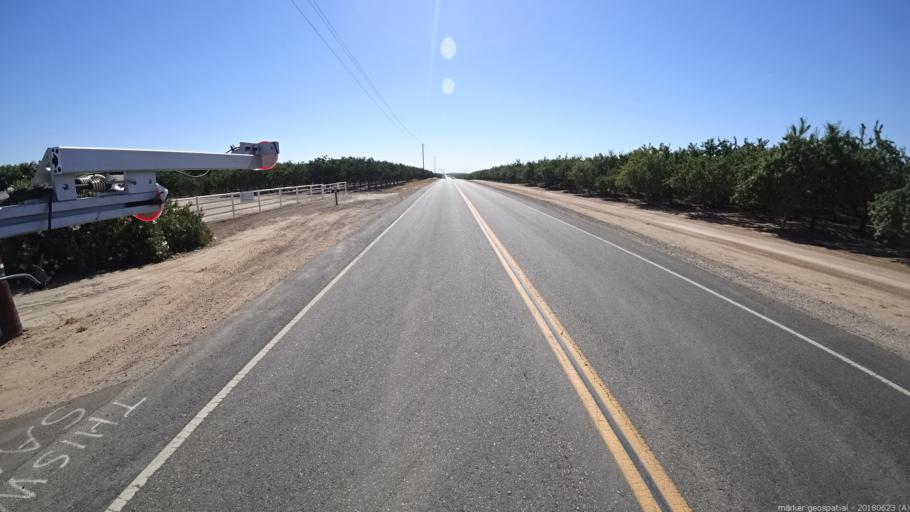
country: US
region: California
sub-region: Madera County
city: Parksdale
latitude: 36.9666
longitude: -119.9560
